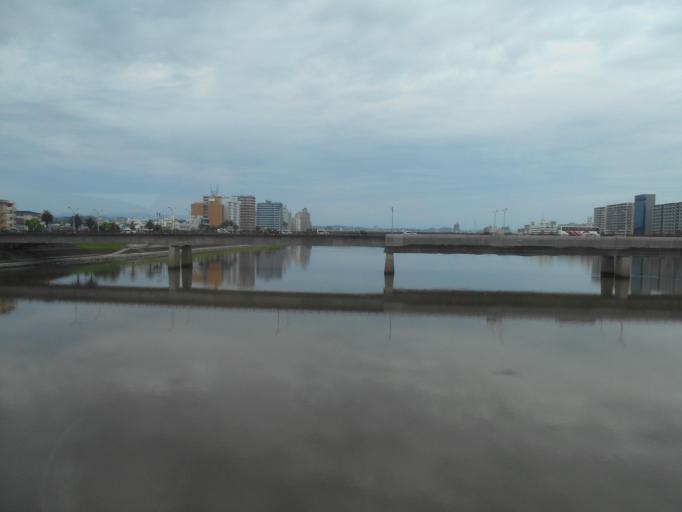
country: JP
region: Miyazaki
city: Miyazaki-shi
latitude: 31.9021
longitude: 131.4282
